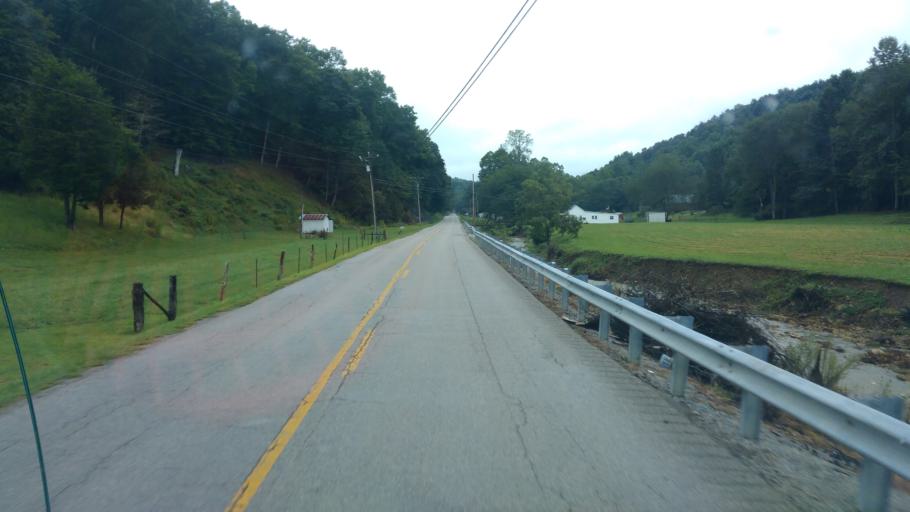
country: US
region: Kentucky
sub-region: Fleming County
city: Flemingsburg
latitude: 38.4498
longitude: -83.5133
